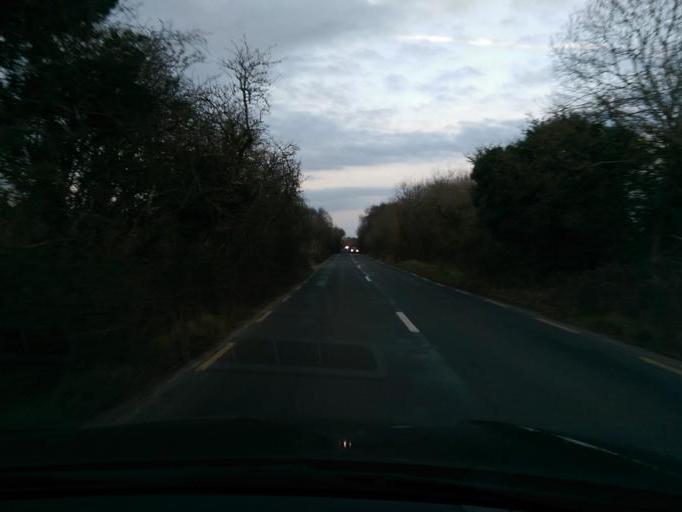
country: IE
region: Connaught
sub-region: County Galway
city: Portumna
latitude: 53.0596
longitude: -8.0949
